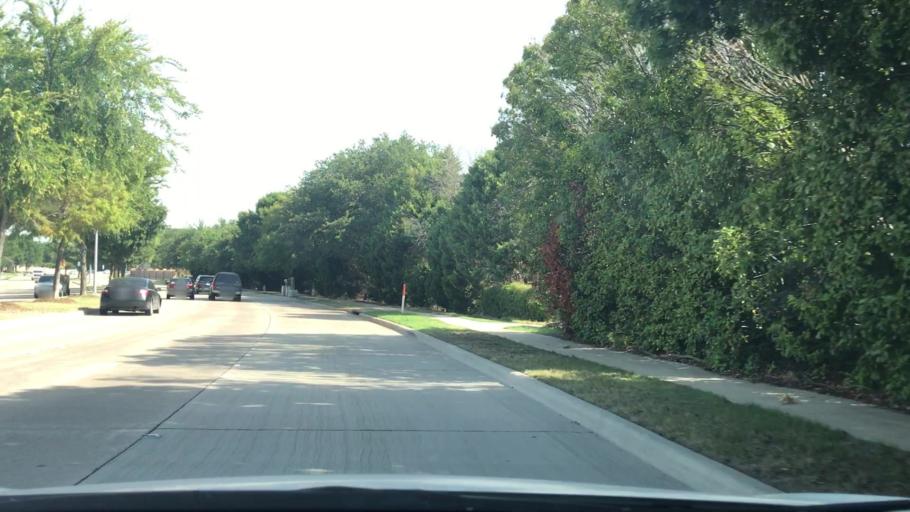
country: US
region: Texas
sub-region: Collin County
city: Allen
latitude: 33.0985
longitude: -96.7503
